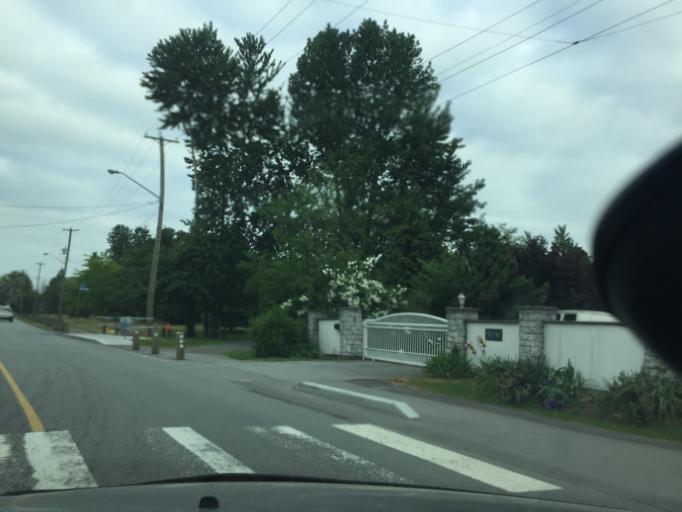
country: CA
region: British Columbia
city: Richmond
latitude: 49.1628
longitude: -123.1199
